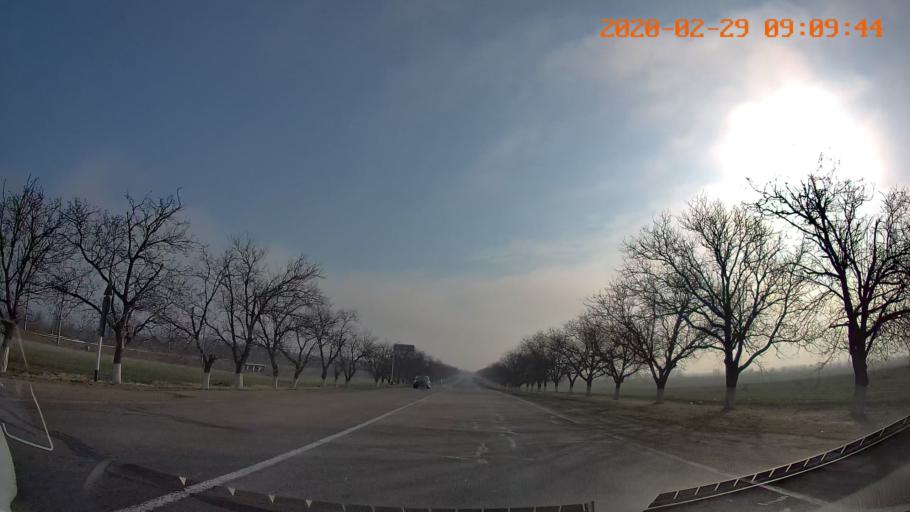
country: MD
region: Telenesti
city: Slobozia
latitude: 46.8449
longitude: 29.7677
